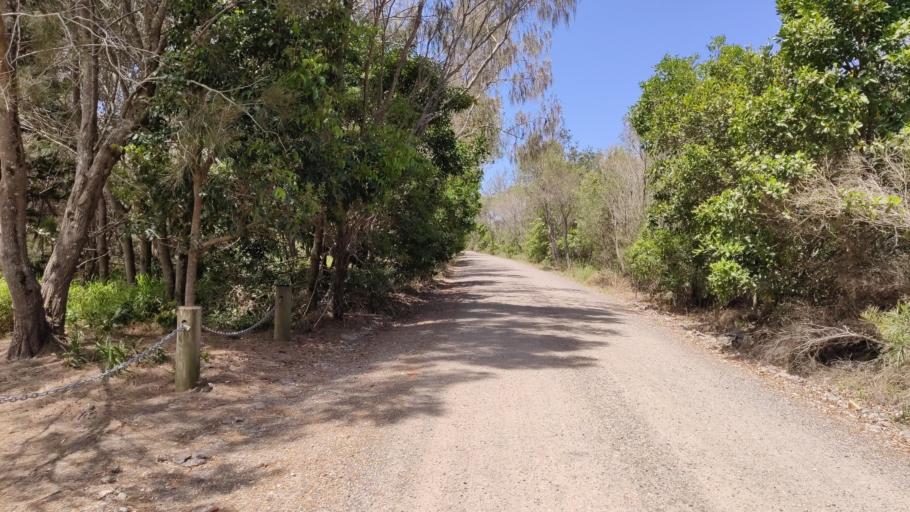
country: AU
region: New South Wales
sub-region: Port Macquarie-Hastings
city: North Haven
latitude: -31.6397
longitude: 152.8281
